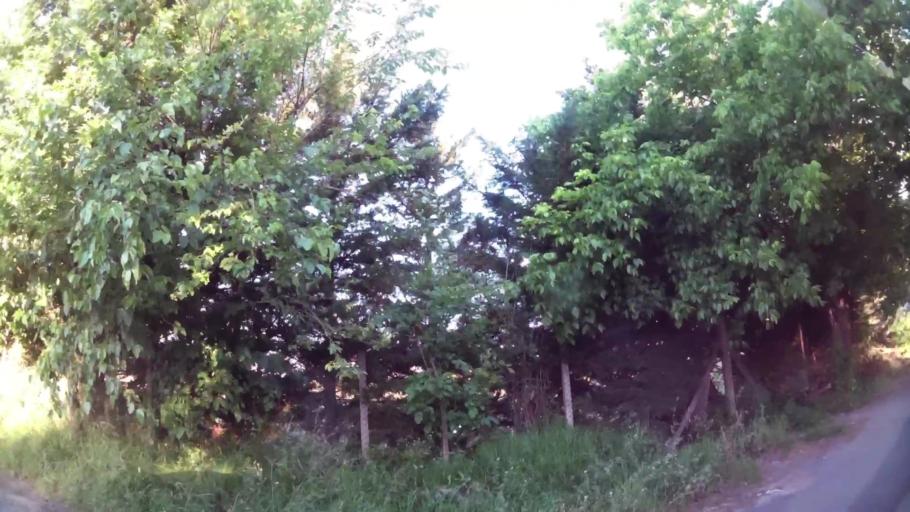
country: AR
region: Buenos Aires
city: Santa Catalina - Dique Lujan
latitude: -34.4655
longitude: -58.7520
